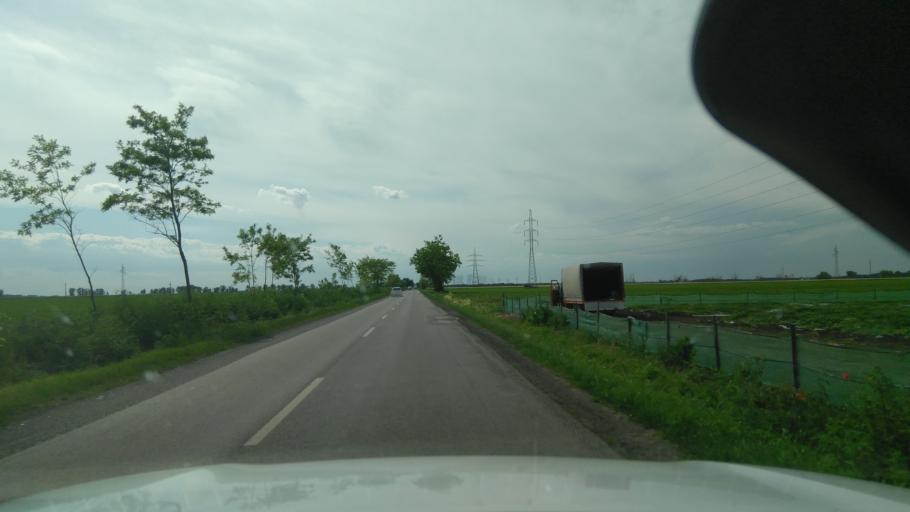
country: HU
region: Bekes
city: Medgyesegyhaza
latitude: 46.5069
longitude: 21.0047
